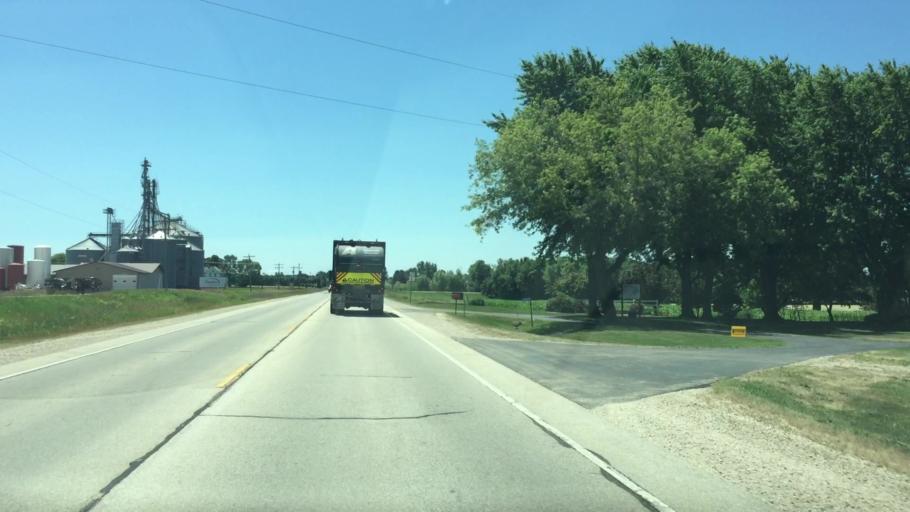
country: US
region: Wisconsin
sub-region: Calumet County
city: Chilton
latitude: 44.0766
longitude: -88.1634
